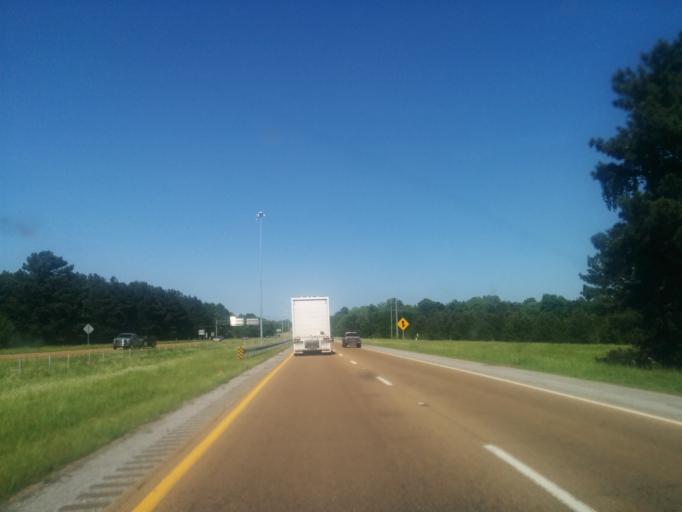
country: US
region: Mississippi
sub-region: Hinds County
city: Jackson
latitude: 32.3606
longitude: -90.2340
